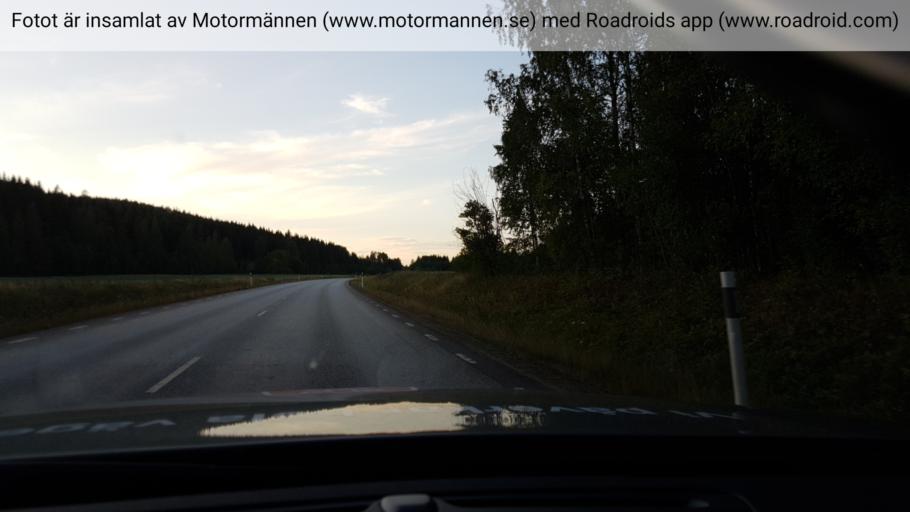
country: SE
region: Vaermland
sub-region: Storfors Kommun
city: Storfors
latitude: 59.5125
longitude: 14.3042
